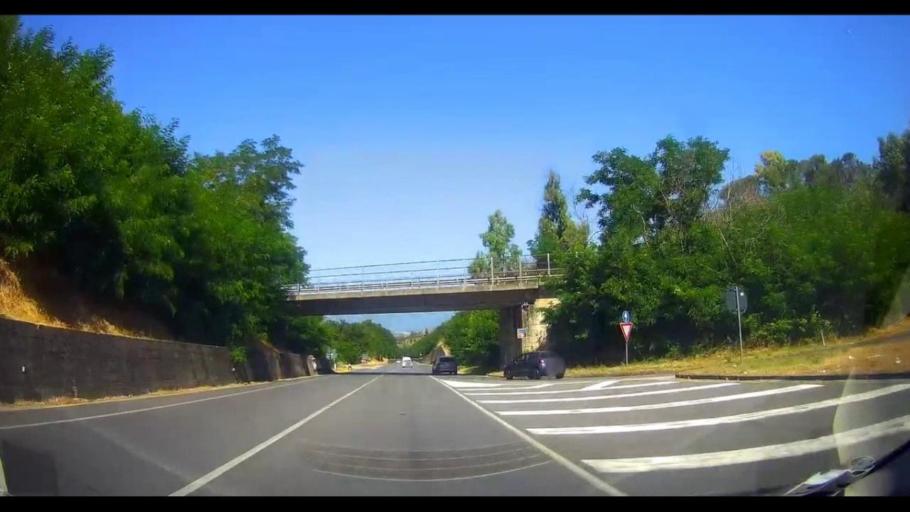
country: IT
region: Calabria
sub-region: Provincia di Cosenza
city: Rovito
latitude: 39.2966
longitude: 16.3045
